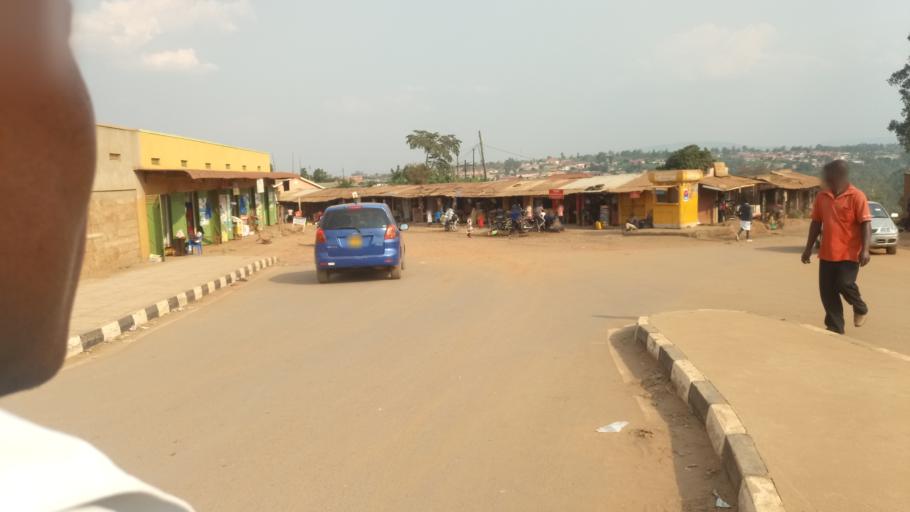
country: UG
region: Western Region
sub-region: Mbarara District
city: Mbarara
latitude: -0.6117
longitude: 30.6660
